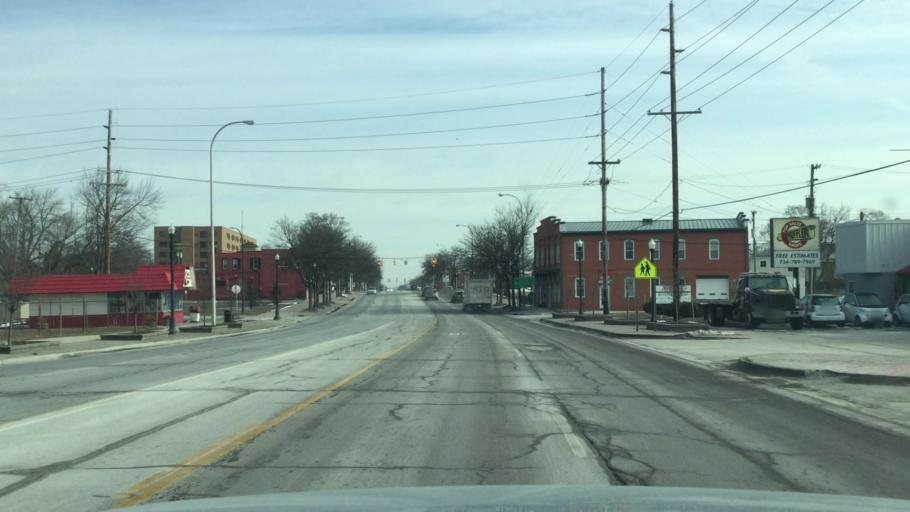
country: US
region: Michigan
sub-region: Wayne County
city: Flat Rock
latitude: 42.0948
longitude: -83.2947
